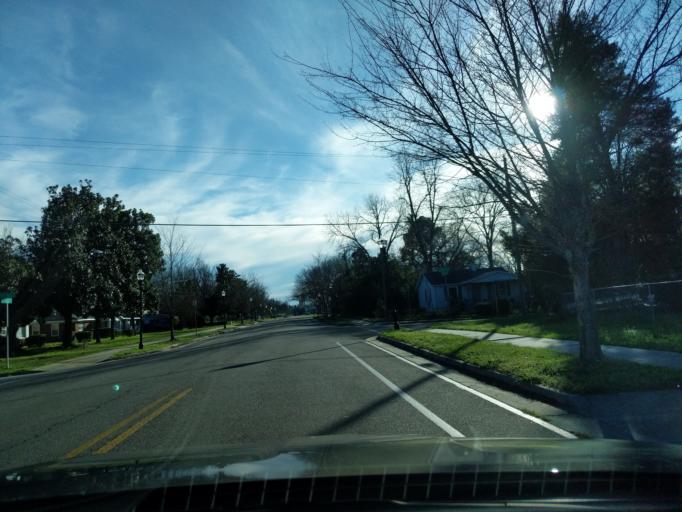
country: US
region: Georgia
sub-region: Richmond County
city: Augusta
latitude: 33.4600
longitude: -81.9525
